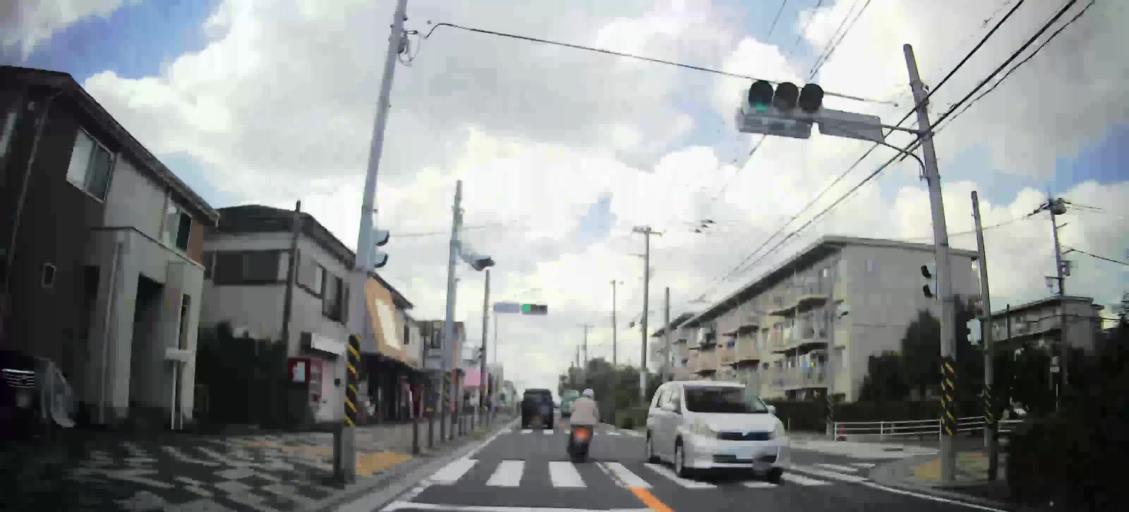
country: JP
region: Kanagawa
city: Yokohama
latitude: 35.4681
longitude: 139.5607
